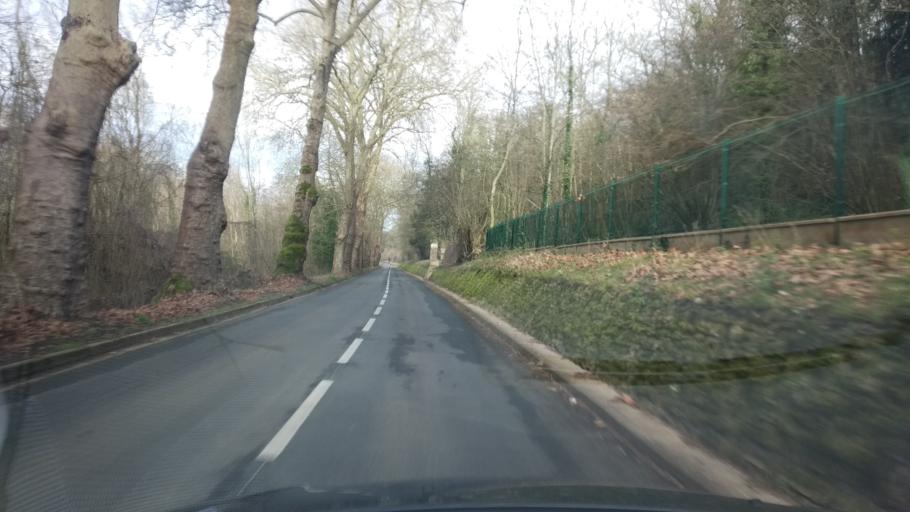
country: FR
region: Poitou-Charentes
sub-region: Departement de la Vienne
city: Poitiers
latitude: 46.6047
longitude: 0.3491
